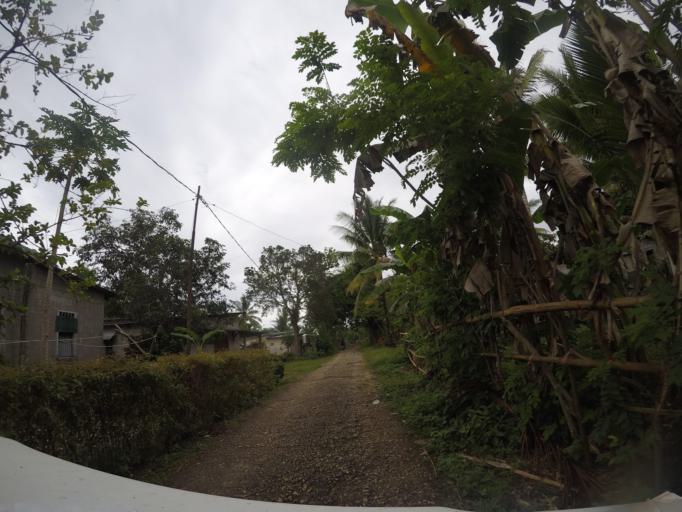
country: TL
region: Lautem
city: Lospalos
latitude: -8.5269
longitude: 126.9956
